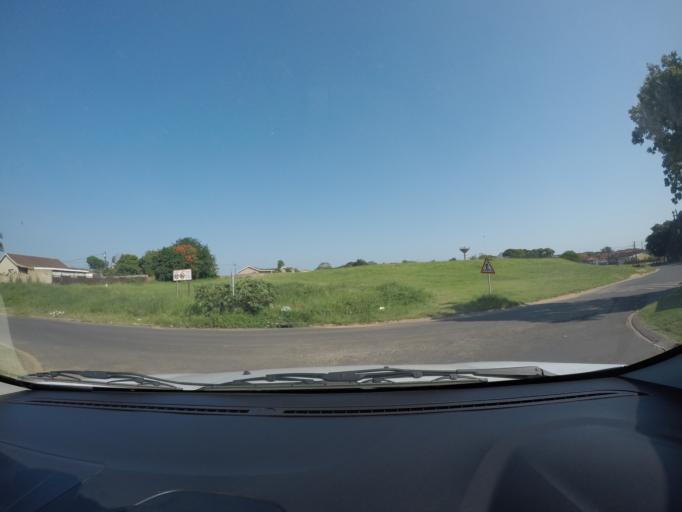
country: ZA
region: KwaZulu-Natal
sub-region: uThungulu District Municipality
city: Richards Bay
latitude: -28.7189
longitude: 32.0397
